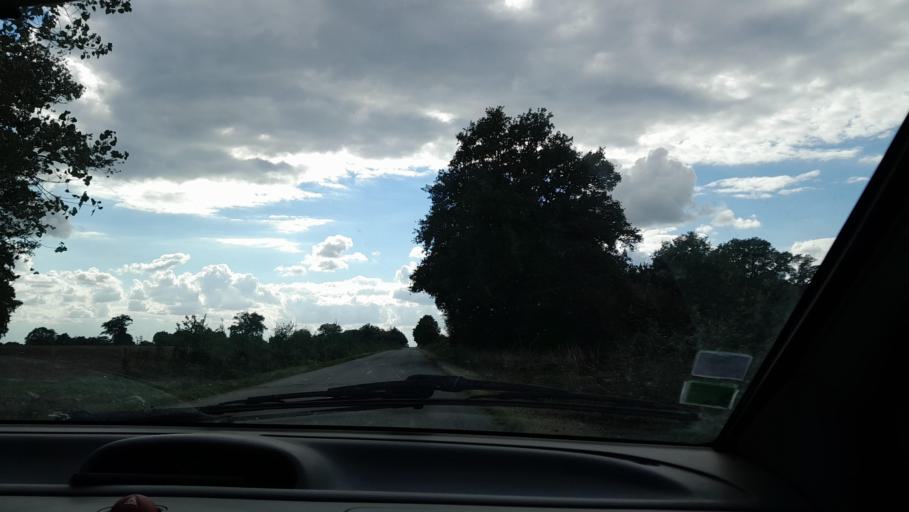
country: FR
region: Brittany
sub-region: Departement d'Ille-et-Vilaine
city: Le Pertre
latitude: 47.9784
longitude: -1.0166
